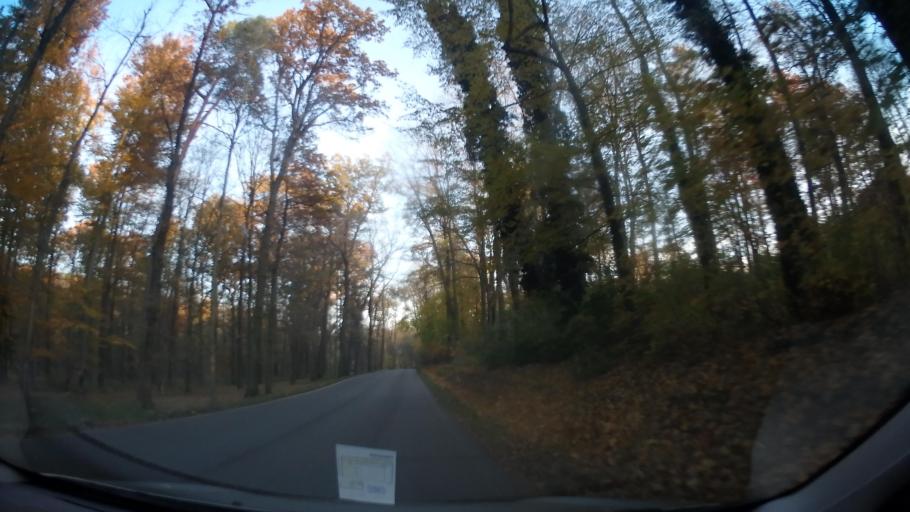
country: CZ
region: Central Bohemia
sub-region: Okres Benesov
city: Benesov
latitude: 49.7822
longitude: 14.6591
